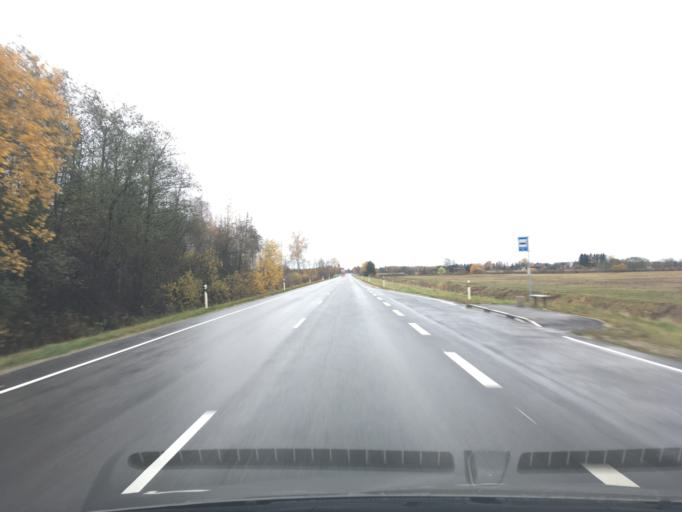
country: EE
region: Jogevamaa
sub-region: Tabivere vald
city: Tabivere
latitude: 58.4409
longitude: 26.5034
